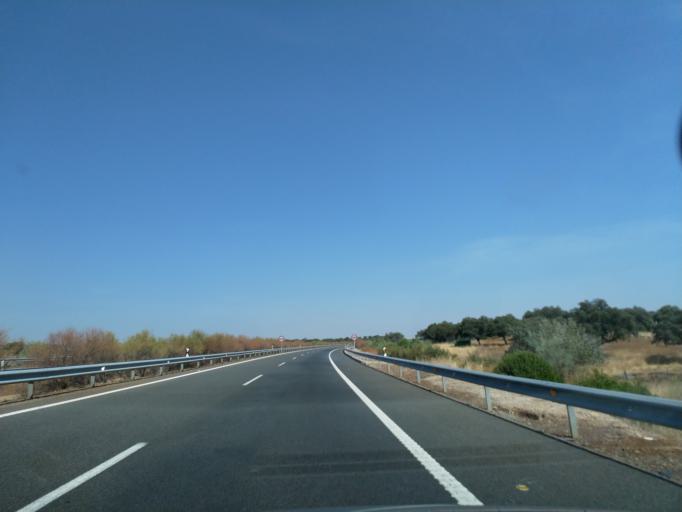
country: ES
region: Extremadura
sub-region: Provincia de Badajoz
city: Mirandilla
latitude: 39.0017
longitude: -6.3312
